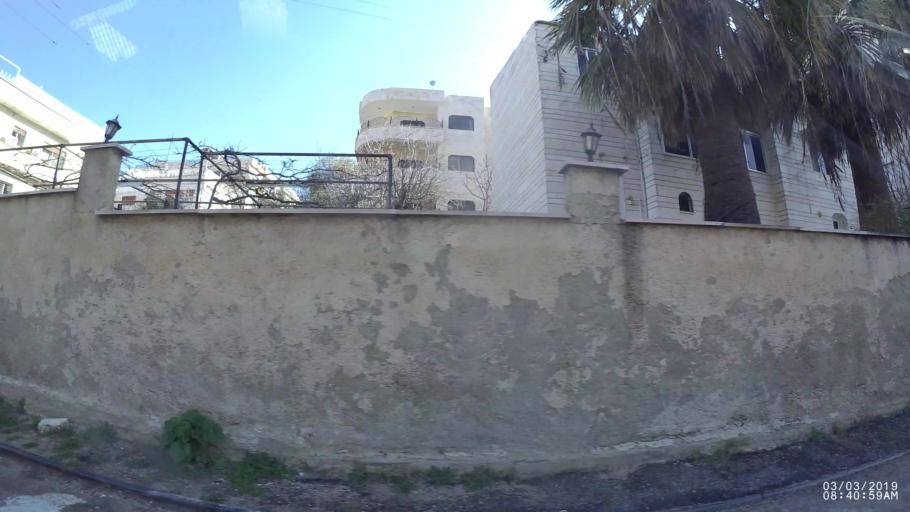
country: JO
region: Amman
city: Al Jubayhah
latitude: 32.0004
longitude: 35.8822
